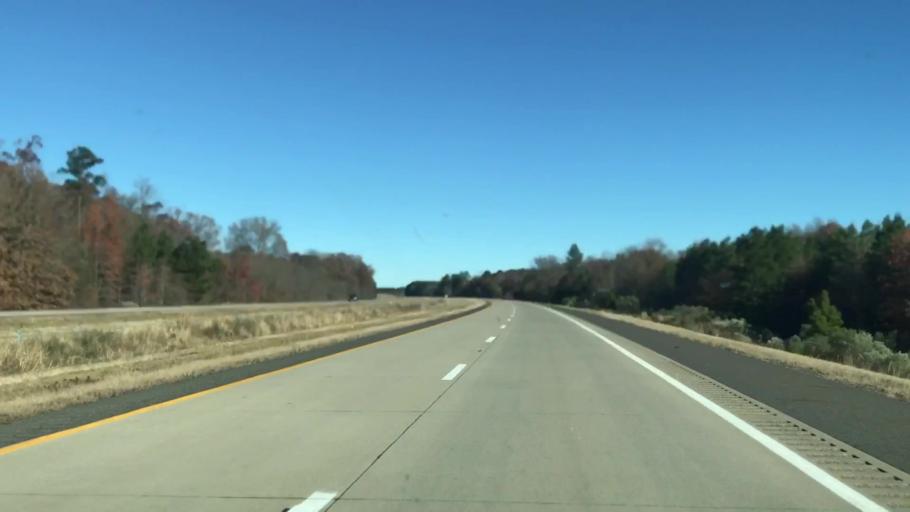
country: US
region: Texas
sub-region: Bowie County
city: Texarkana
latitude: 33.2100
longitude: -93.8744
